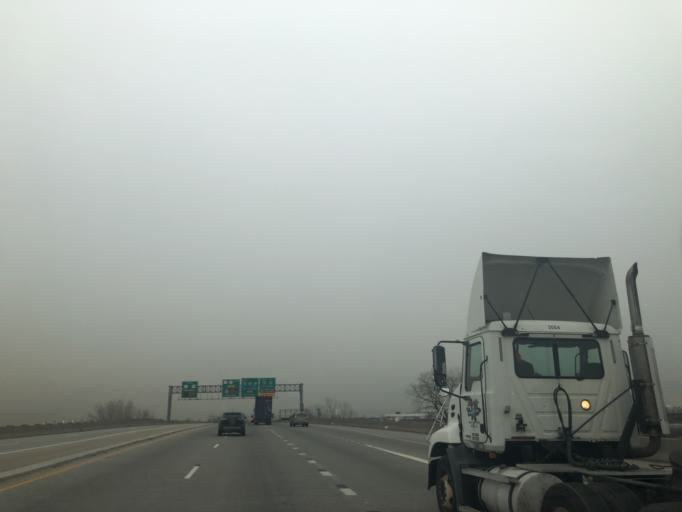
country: US
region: New Jersey
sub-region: Essex County
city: Newark
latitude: 40.7144
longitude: -74.1566
